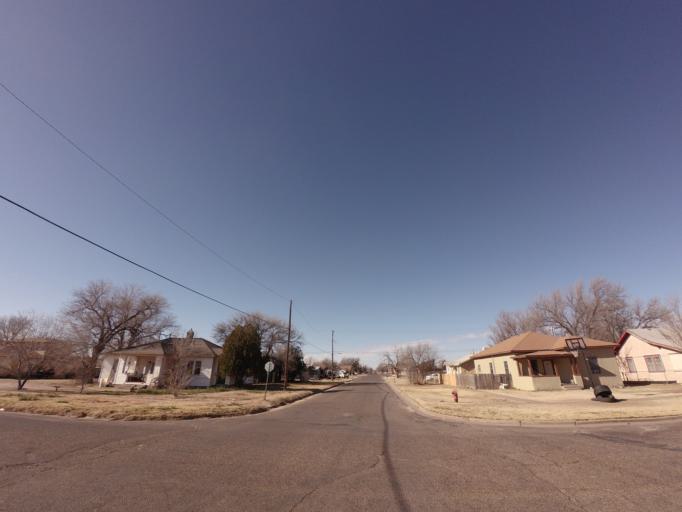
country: US
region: New Mexico
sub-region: Curry County
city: Clovis
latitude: 34.4068
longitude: -103.2079
